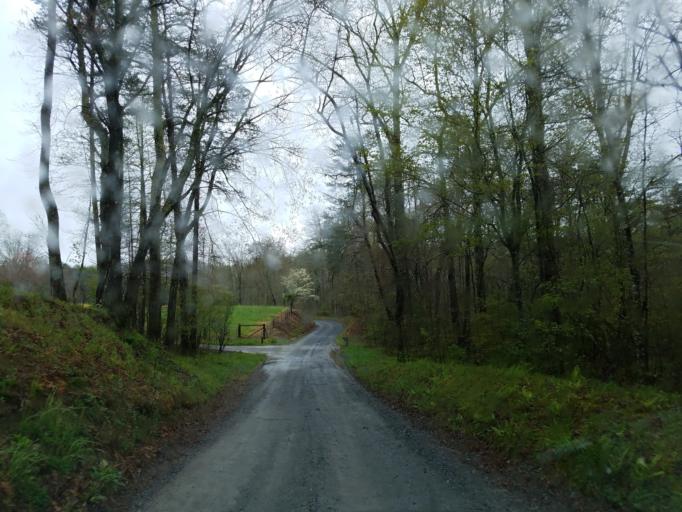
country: US
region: Georgia
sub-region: Fannin County
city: Blue Ridge
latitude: 34.8573
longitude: -84.2335
